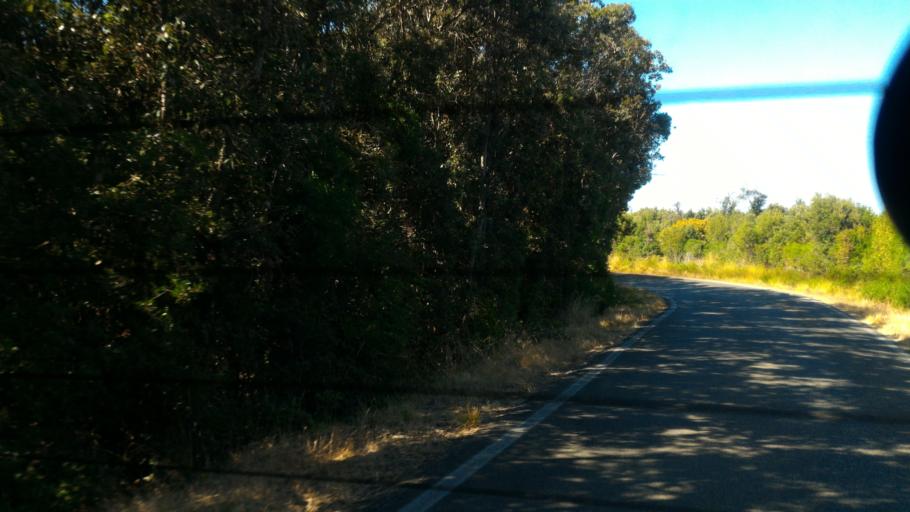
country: IT
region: Tuscany
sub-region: Provincia di Grosseto
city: Porto Ercole
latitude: 42.4271
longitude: 11.1731
